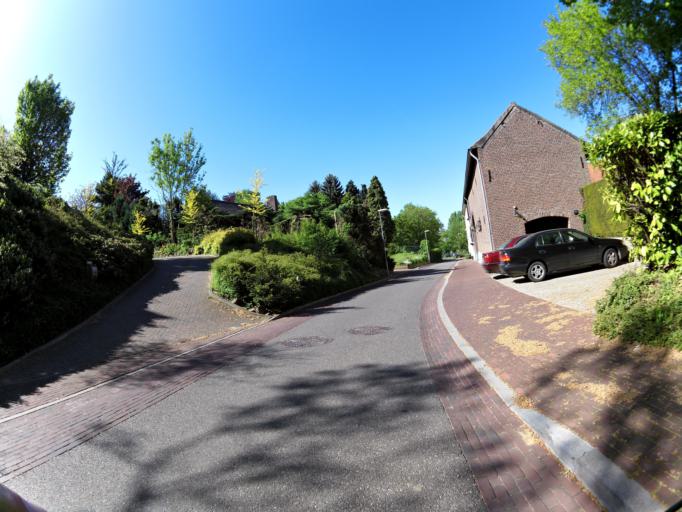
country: NL
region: Limburg
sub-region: Gemeente Schinnen
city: Schinnen
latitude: 50.9373
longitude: 5.8957
